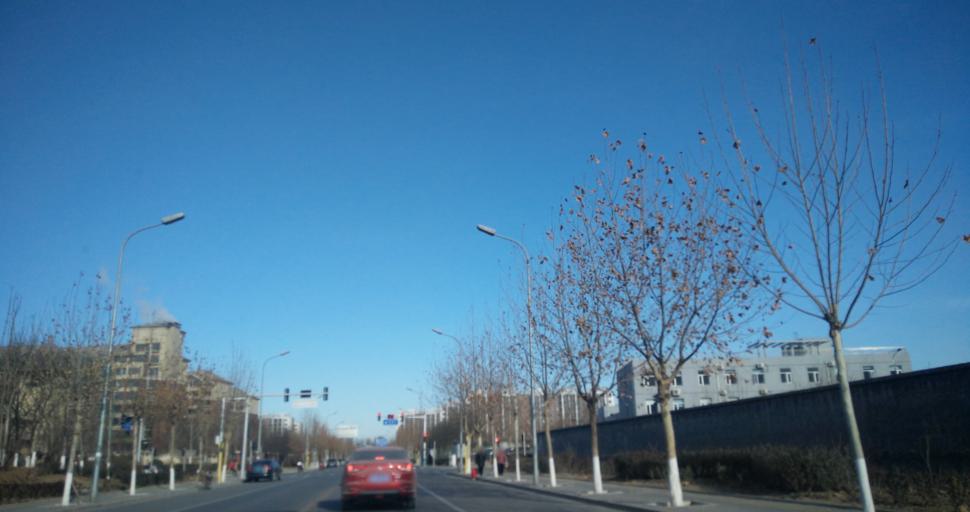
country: CN
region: Beijing
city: Yinghai
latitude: 39.7119
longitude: 116.3972
